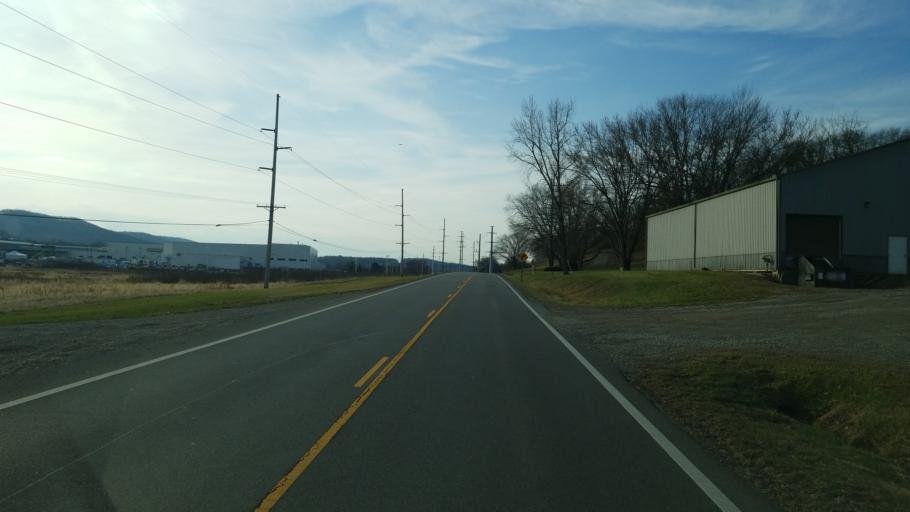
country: US
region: Ohio
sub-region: Ross County
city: Chillicothe
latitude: 39.4040
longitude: -82.9607
